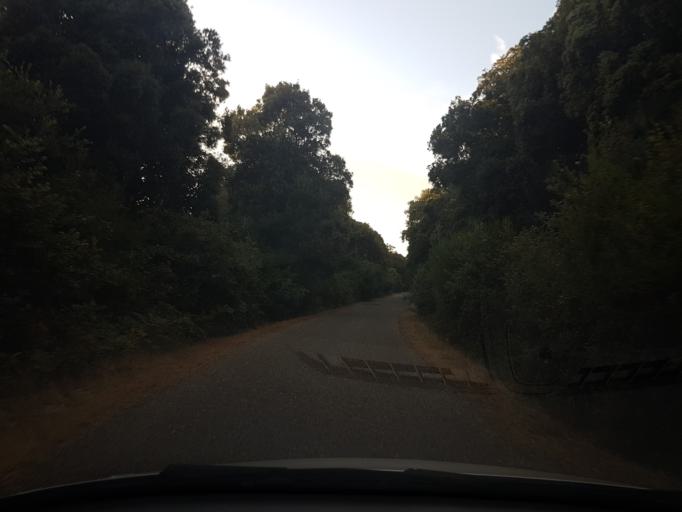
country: IT
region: Sardinia
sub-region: Provincia di Oristano
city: Seneghe
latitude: 40.1071
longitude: 8.5891
